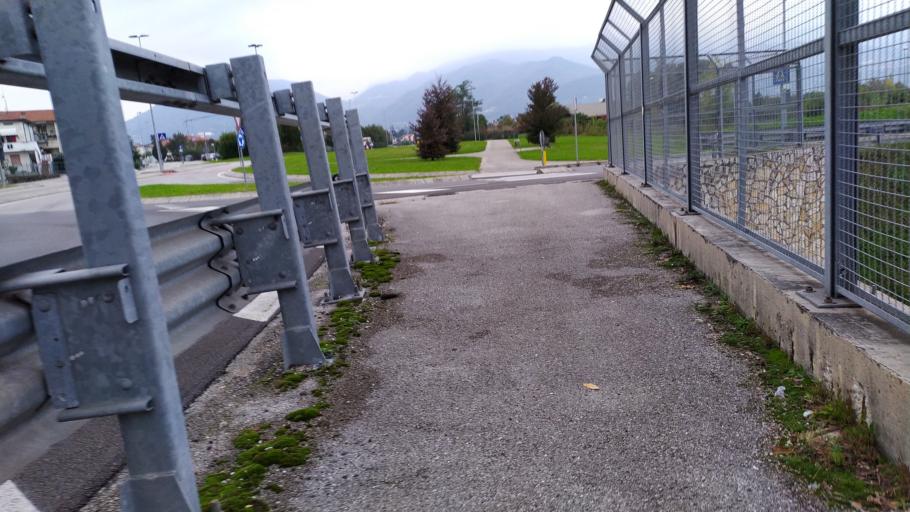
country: IT
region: Veneto
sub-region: Provincia di Vicenza
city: Schio
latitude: 45.7013
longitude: 11.3665
